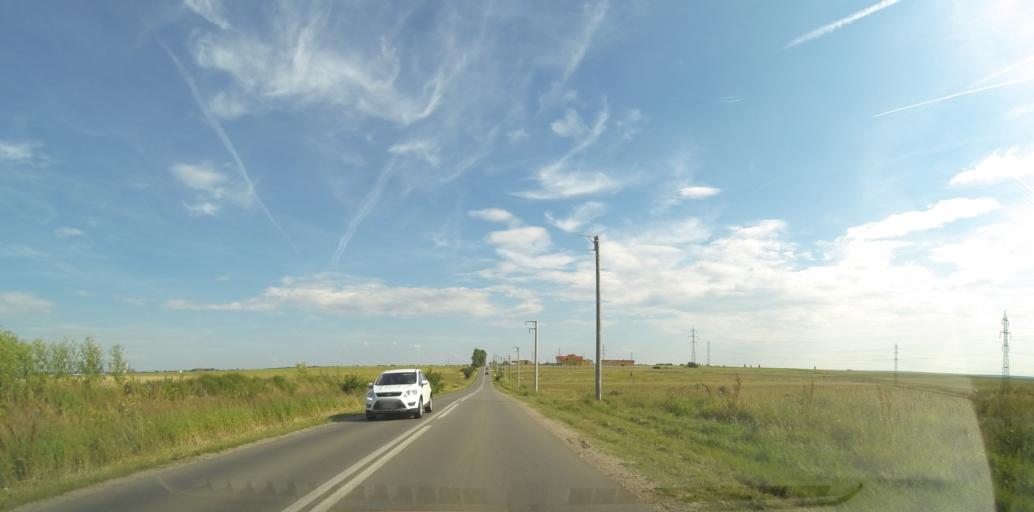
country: RO
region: Dolj
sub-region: Comuna Simnicu de Sus
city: Simnicu de Sus
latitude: 44.3584
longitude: 23.7849
